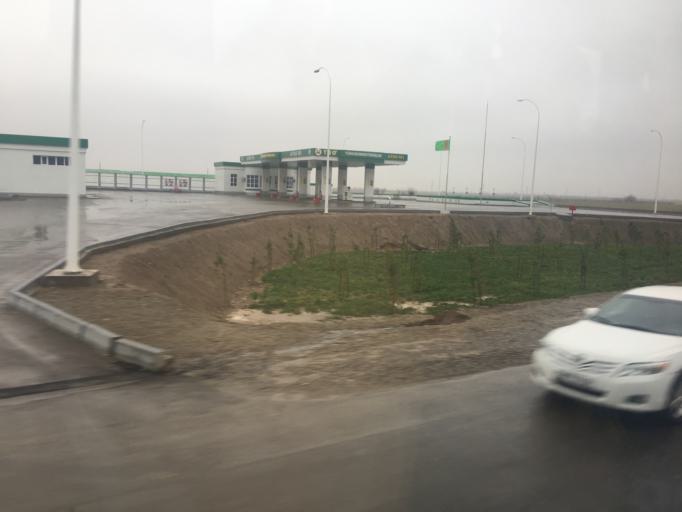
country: TM
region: Lebap
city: Turkmenabat
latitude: 39.0093
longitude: 63.5950
